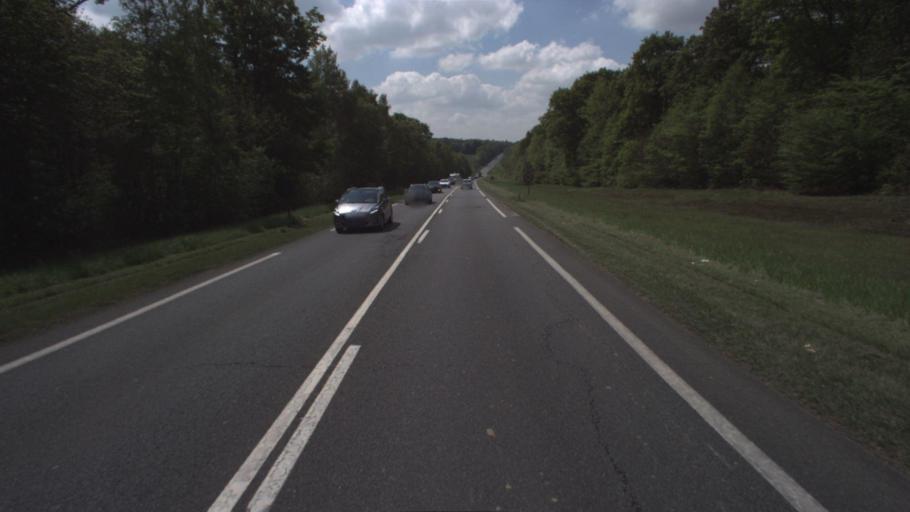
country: FR
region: Ile-de-France
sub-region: Departement de Seine-et-Marne
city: Chaumes-en-Brie
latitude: 48.6637
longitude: 2.8103
